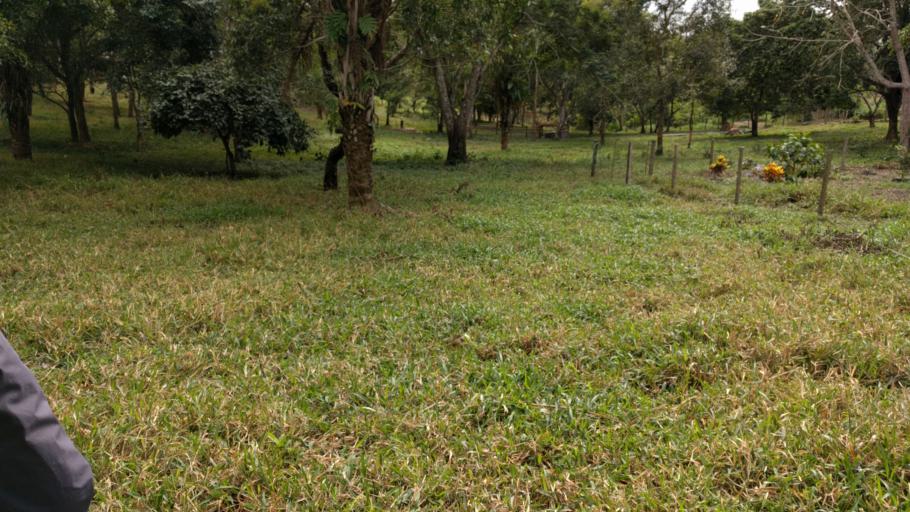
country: BO
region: Santa Cruz
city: San Juan del Surutu
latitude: -17.4603
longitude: -63.6967
